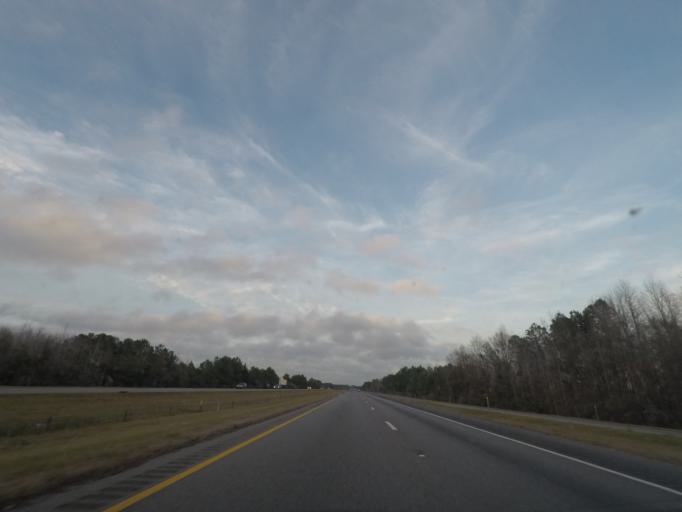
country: US
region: South Carolina
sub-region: Orangeburg County
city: Holly Hill
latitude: 33.3858
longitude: -80.5173
